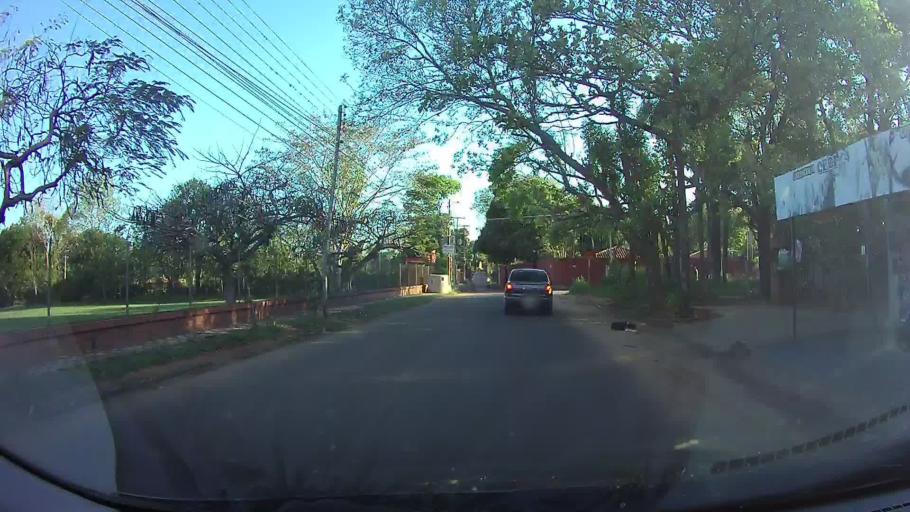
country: PY
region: Central
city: Fernando de la Mora
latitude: -25.3433
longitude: -57.5324
